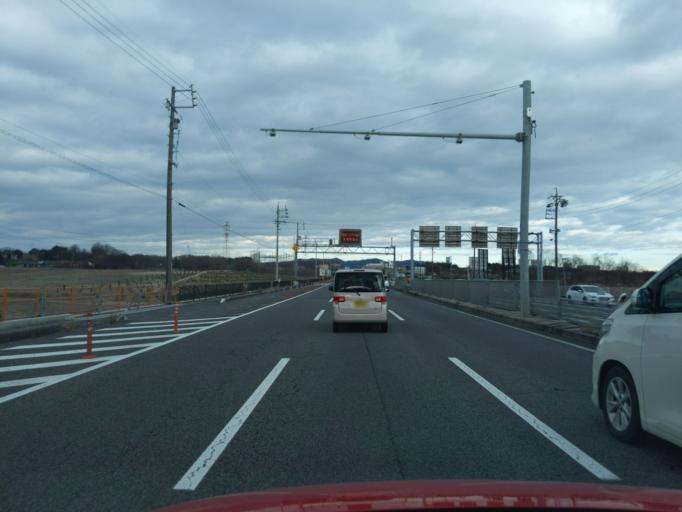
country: JP
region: Aichi
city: Kasugai
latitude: 35.2705
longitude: 136.9997
